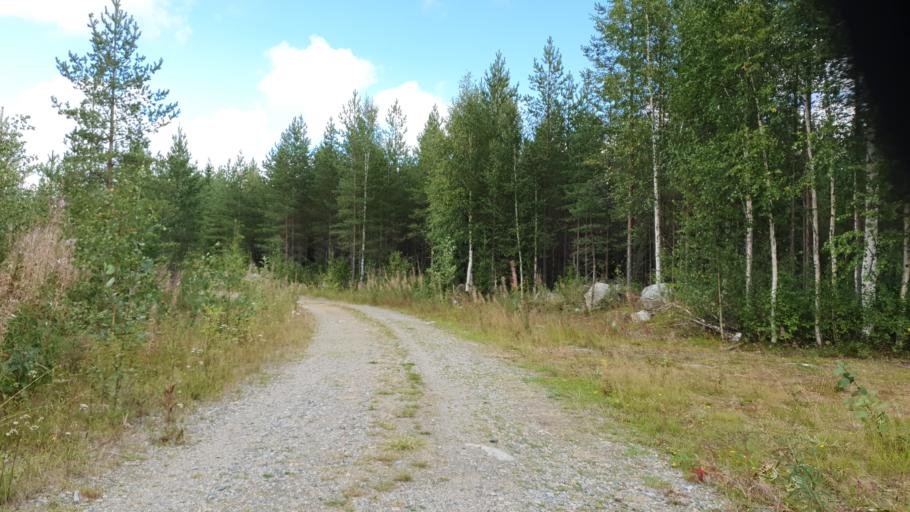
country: FI
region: Kainuu
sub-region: Kehys-Kainuu
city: Kuhmo
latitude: 64.1451
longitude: 29.3871
